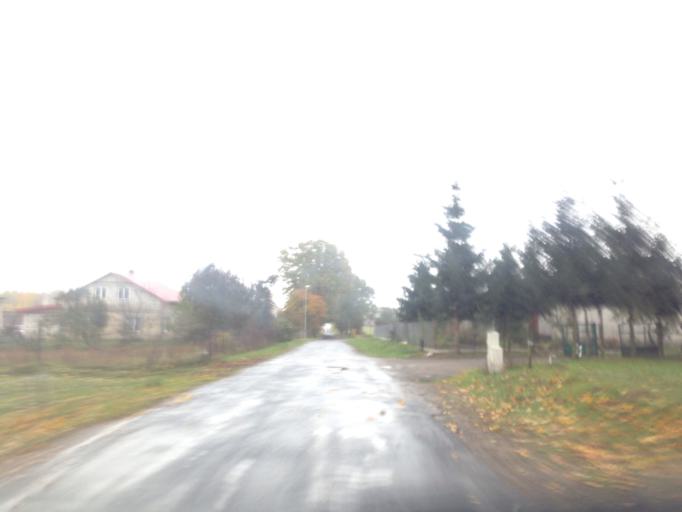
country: PL
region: Warmian-Masurian Voivodeship
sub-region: Powiat nowomiejski
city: Biskupiec
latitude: 53.5790
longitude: 19.4350
